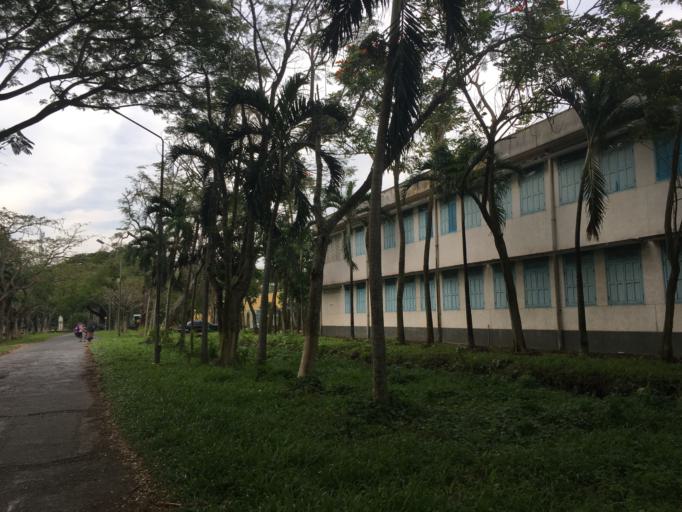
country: VN
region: Can Tho
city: Can Tho
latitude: 10.0315
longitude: 105.7701
